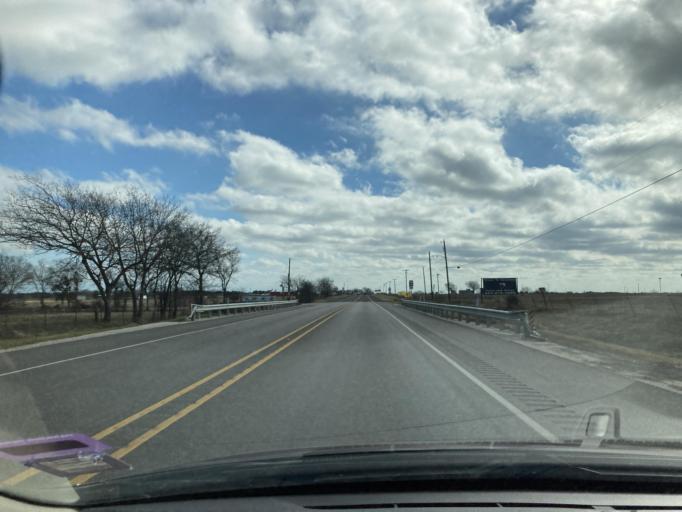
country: US
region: Texas
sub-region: Navarro County
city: Corsicana
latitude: 32.0435
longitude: -96.4126
